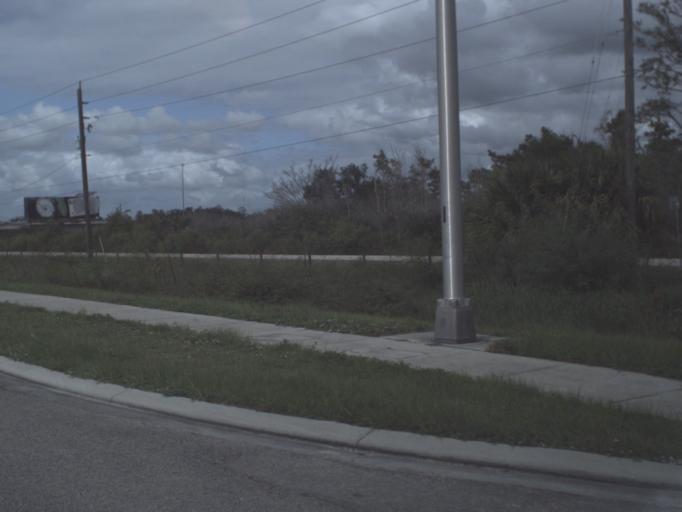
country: US
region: Florida
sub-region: Lee County
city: Fort Myers
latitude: 26.6337
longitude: -81.7983
